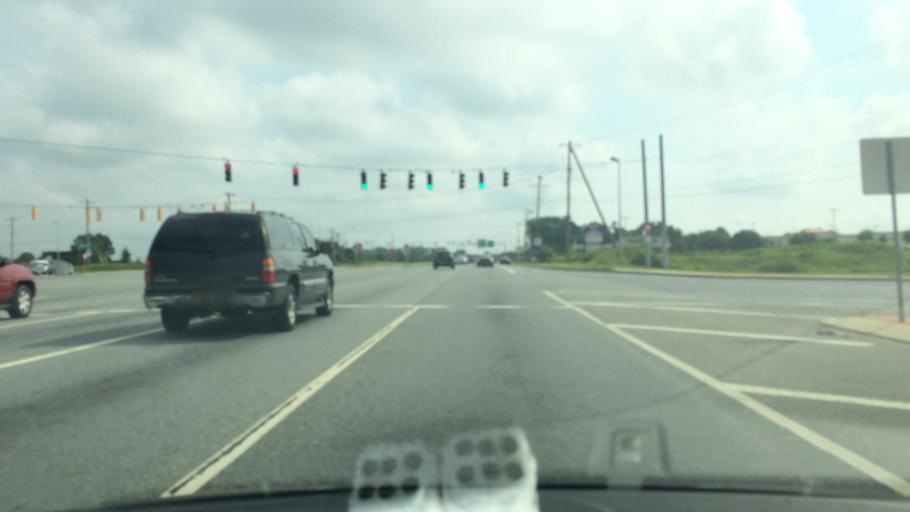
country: US
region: Delaware
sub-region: New Castle County
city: Bear
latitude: 39.6326
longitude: -75.6602
